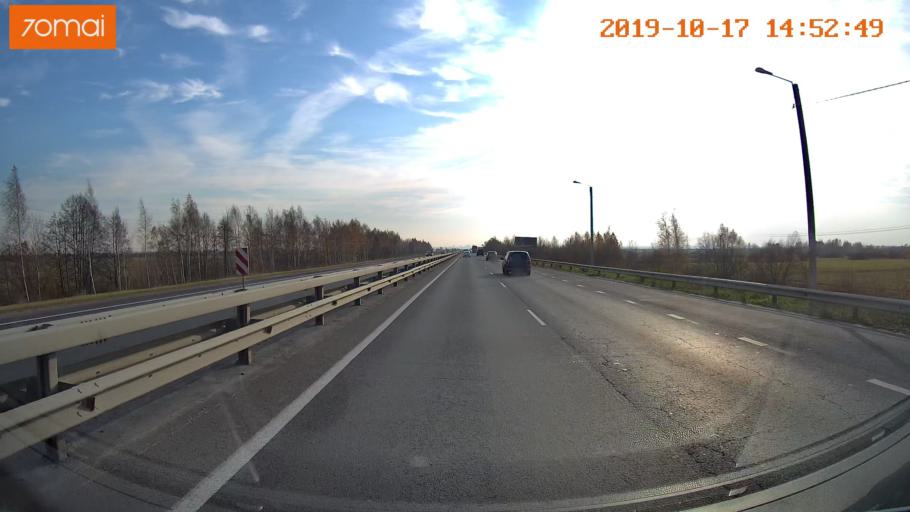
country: RU
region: Rjazan
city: Polyany
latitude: 54.7024
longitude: 39.8429
